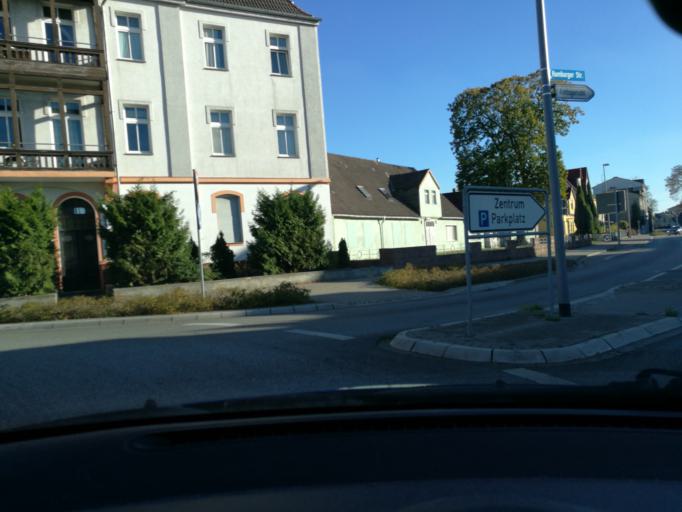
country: DE
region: Brandenburg
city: Perleberg
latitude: 53.0821
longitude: 11.8598
